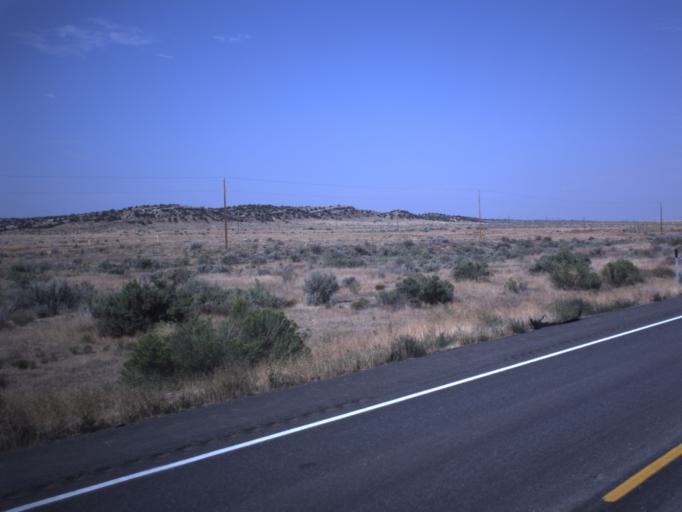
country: US
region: Utah
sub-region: Uintah County
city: Naples
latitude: 40.2997
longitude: -109.1922
